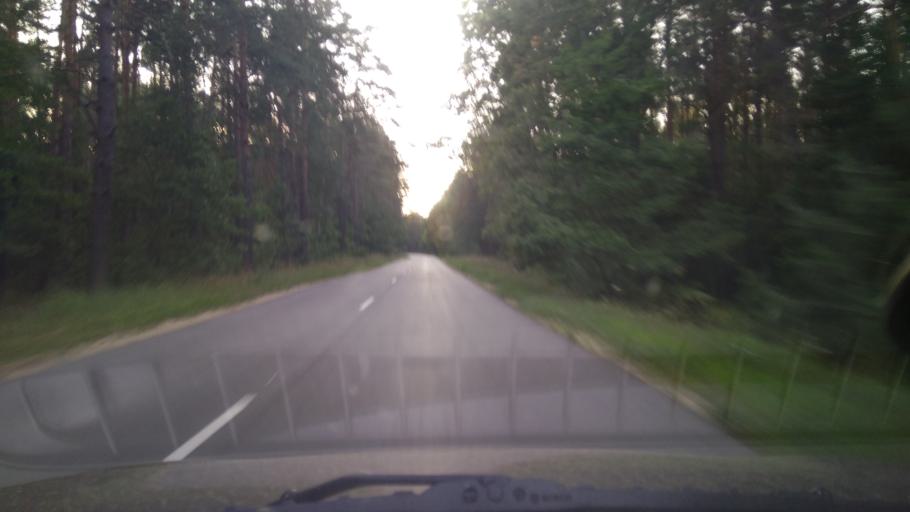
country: BY
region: Brest
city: Nyakhachava
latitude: 52.5964
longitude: 25.1030
